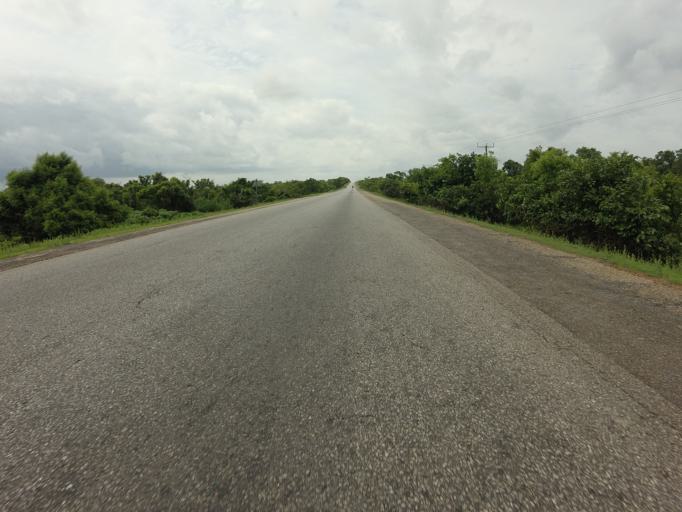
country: GH
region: Brong-Ahafo
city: Kintampo
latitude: 8.6669
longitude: -1.5179
